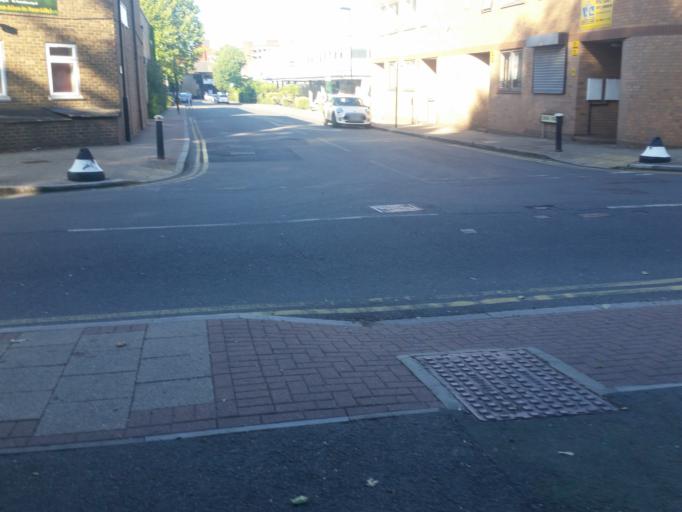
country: GB
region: England
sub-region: Greater London
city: Wood Green
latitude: 51.5934
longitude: -0.1154
